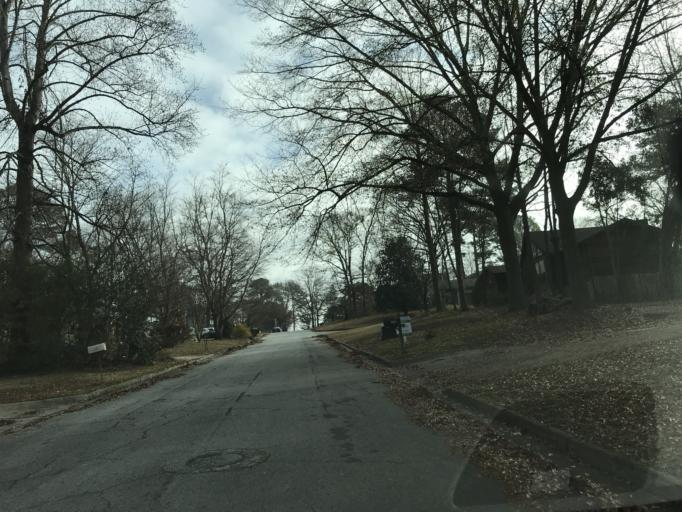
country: US
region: Georgia
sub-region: Clayton County
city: Riverdale
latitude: 33.5576
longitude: -84.3751
